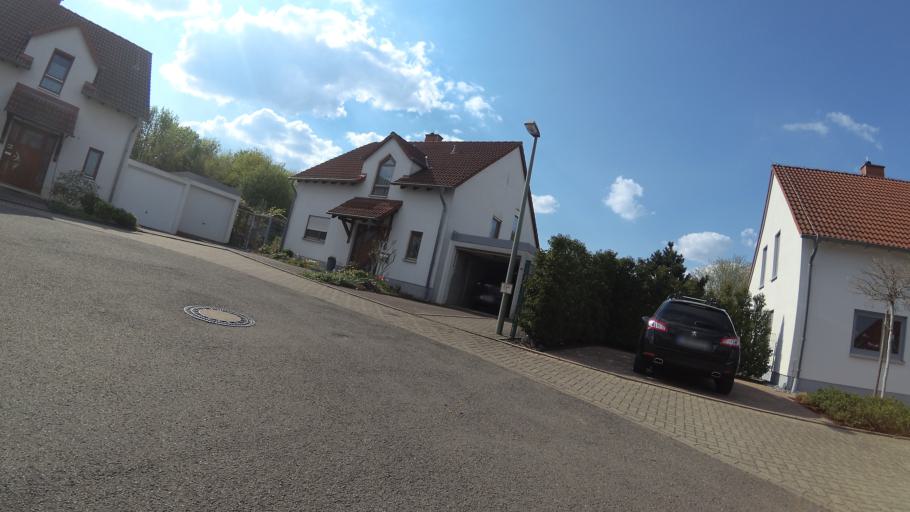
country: DE
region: Saarland
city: Riegelsberg
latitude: 49.3001
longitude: 6.9261
